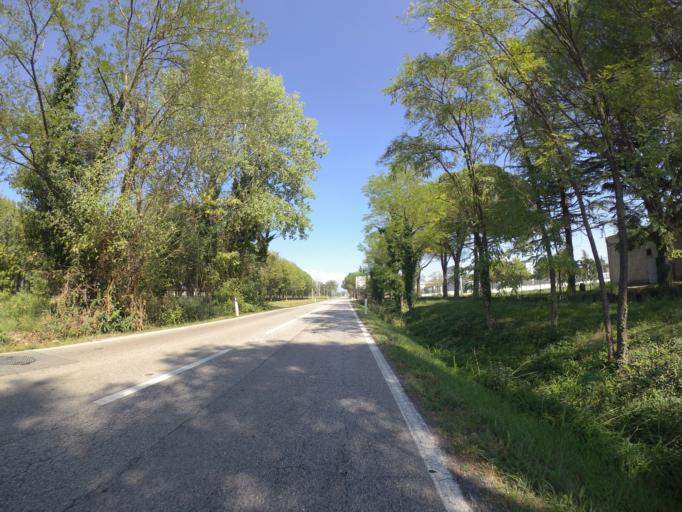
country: IT
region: Friuli Venezia Giulia
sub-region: Provincia di Udine
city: Codroipo
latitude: 45.9746
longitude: 12.9885
